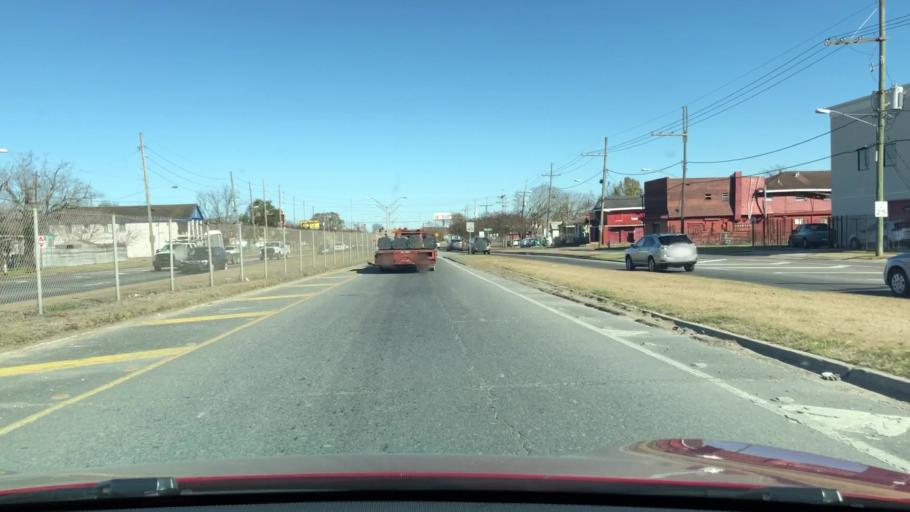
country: US
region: Louisiana
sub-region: Jefferson Parish
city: Jefferson
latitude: 29.9643
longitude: -90.1567
